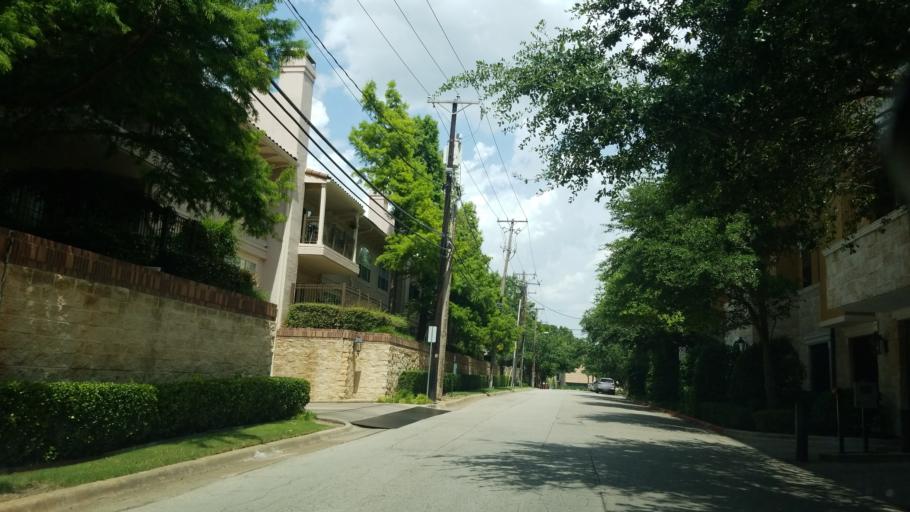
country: US
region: Texas
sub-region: Dallas County
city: University Park
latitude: 32.8678
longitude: -96.7895
